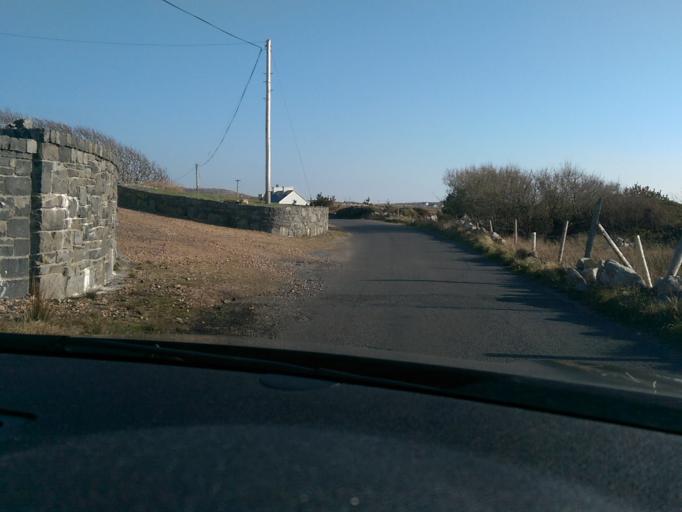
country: IE
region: Connaught
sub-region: County Galway
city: Clifden
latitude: 53.3576
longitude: -9.8762
